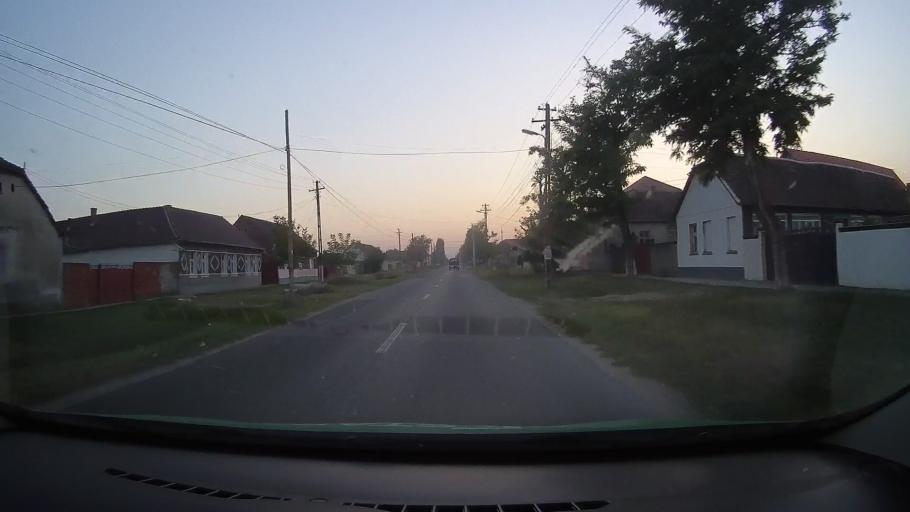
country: RO
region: Arad
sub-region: Comuna Santana
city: Santana
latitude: 46.3557
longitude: 21.5171
